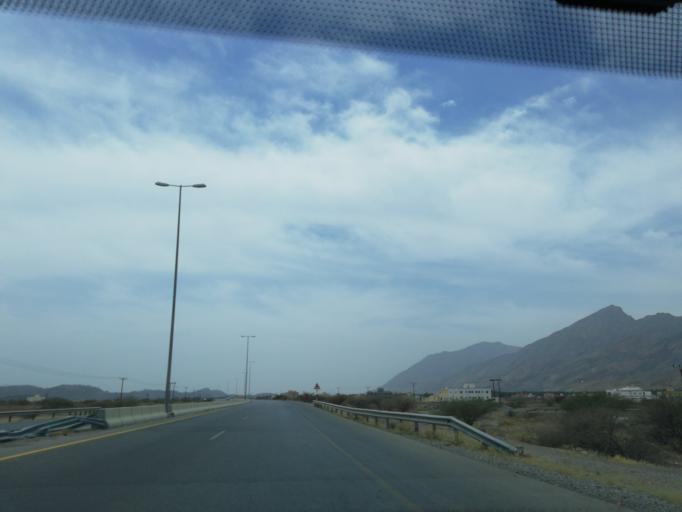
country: OM
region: Muhafazat ad Dakhiliyah
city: Izki
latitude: 23.0163
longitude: 57.7923
